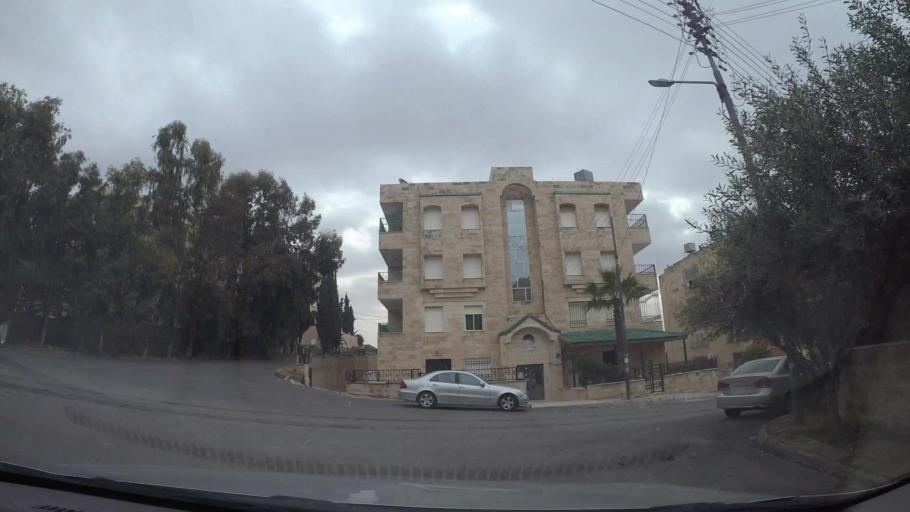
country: JO
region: Amman
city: Umm as Summaq
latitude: 31.9005
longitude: 35.8453
